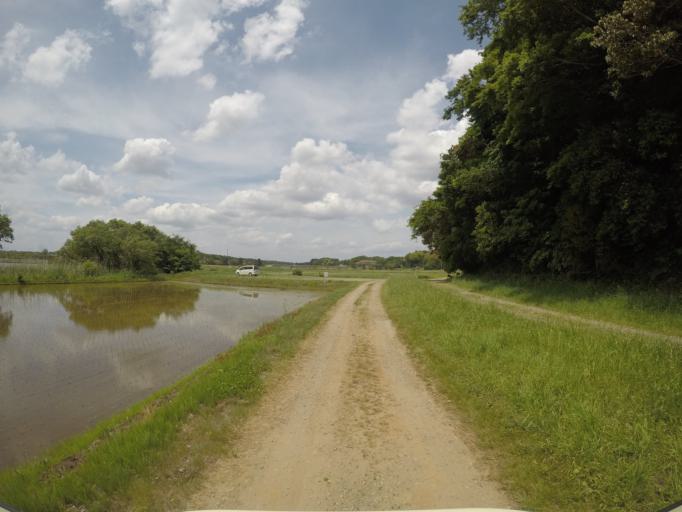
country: JP
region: Ibaraki
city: Ushiku
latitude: 35.9569
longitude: 140.1271
